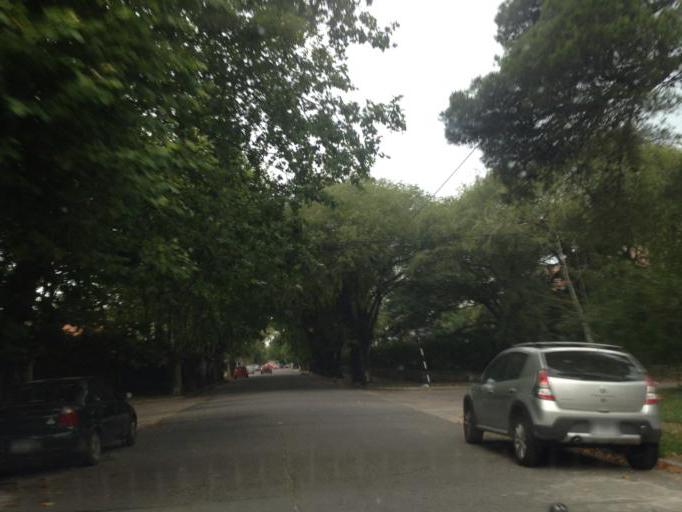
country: AR
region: Buenos Aires
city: Mar del Plata
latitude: -38.0232
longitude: -57.5510
